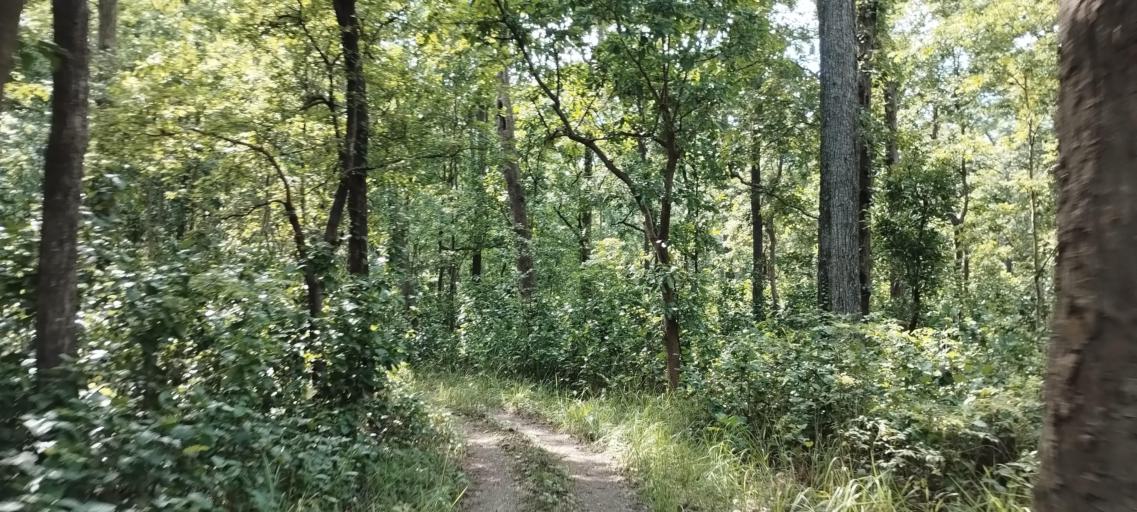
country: NP
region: Far Western
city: Tikapur
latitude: 28.5667
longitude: 81.2867
